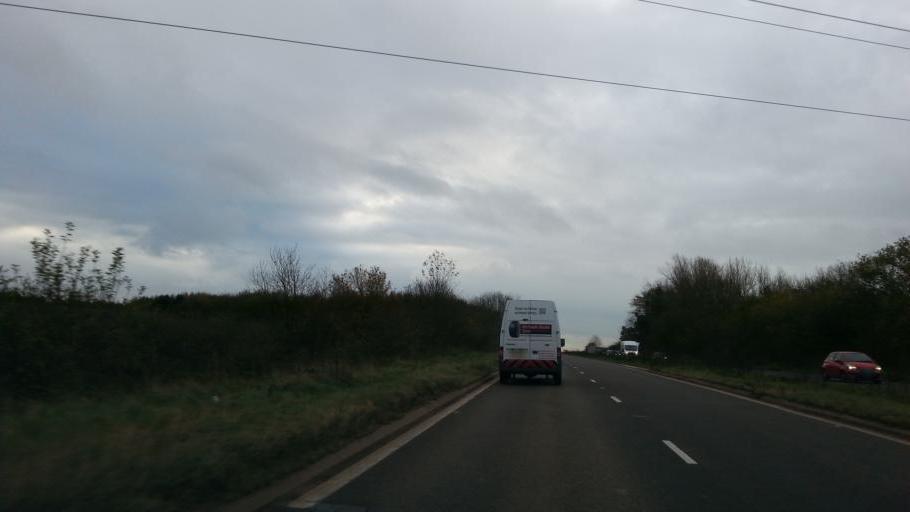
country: GB
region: England
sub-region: Northamptonshire
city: Kettering
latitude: 52.4322
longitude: -0.7343
